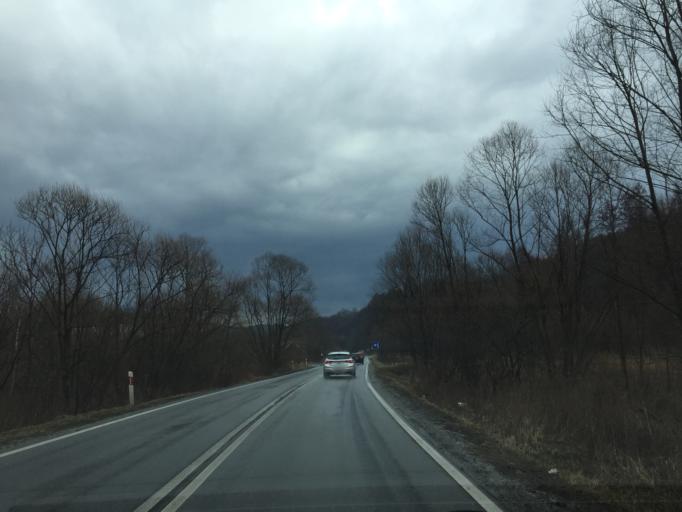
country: PL
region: Lesser Poland Voivodeship
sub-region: Powiat suski
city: Zembrzyce
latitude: 49.7704
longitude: 19.6197
